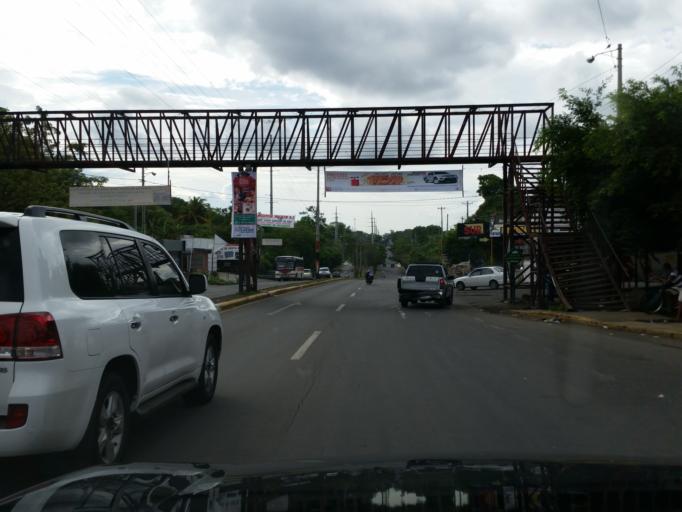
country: NI
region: Masaya
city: Ticuantepe
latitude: 12.0561
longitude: -86.2032
